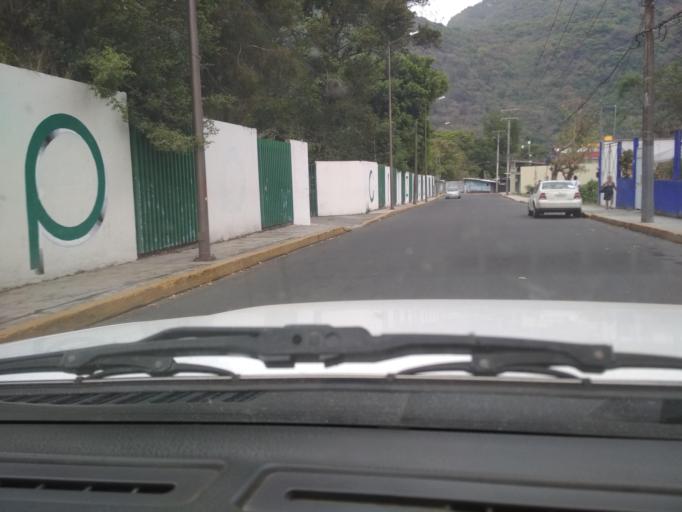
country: MX
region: Veracruz
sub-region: Mariano Escobedo
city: Palmira
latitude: 18.8704
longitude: -97.0967
